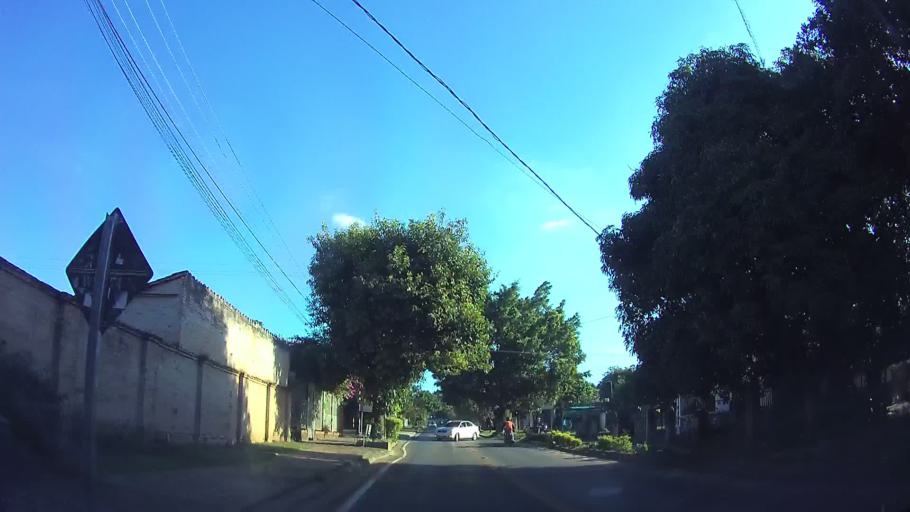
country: PY
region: Central
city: Aregua
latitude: -25.3131
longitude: -57.3782
